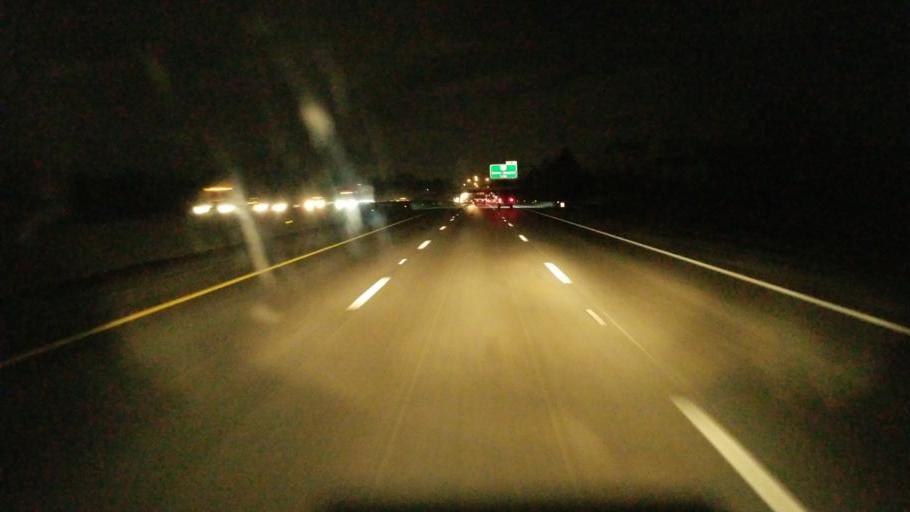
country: US
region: Ohio
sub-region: Clark County
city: Park Layne
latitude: 39.8663
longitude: -84.0750
